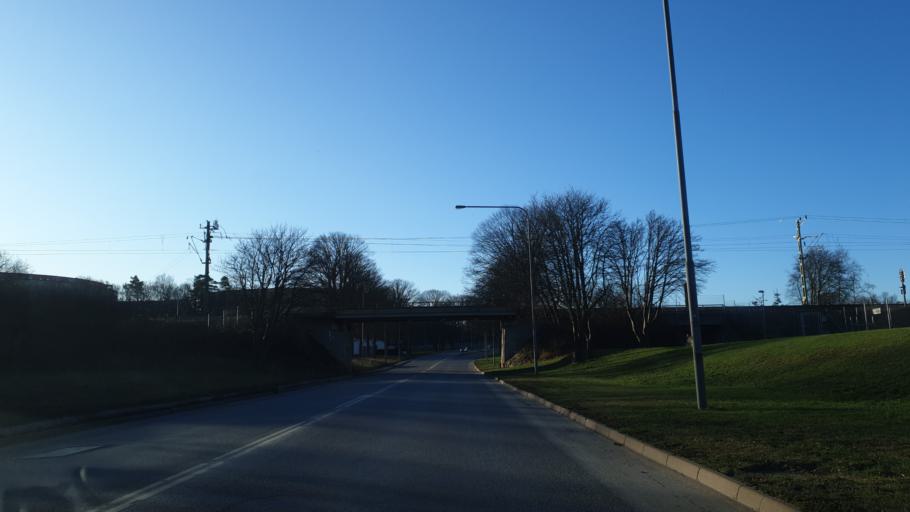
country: SE
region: Blekinge
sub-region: Karlskrona Kommun
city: Karlskrona
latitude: 56.2005
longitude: 15.6225
